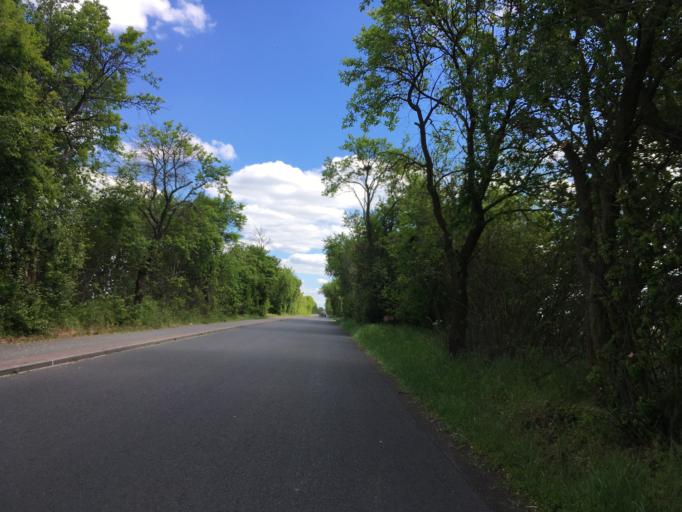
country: DE
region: Brandenburg
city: Wandlitz
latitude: 52.7880
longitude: 13.4670
